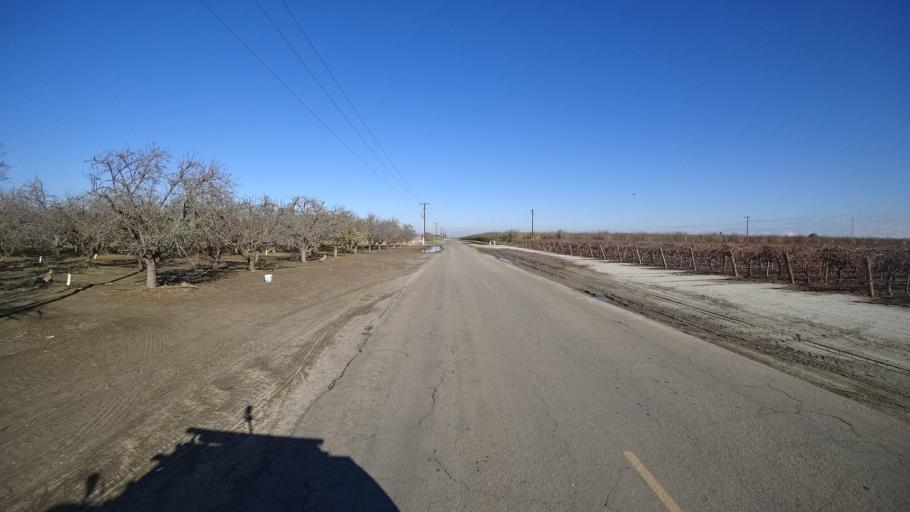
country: US
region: California
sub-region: Kern County
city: Delano
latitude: 35.7351
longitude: -119.2763
